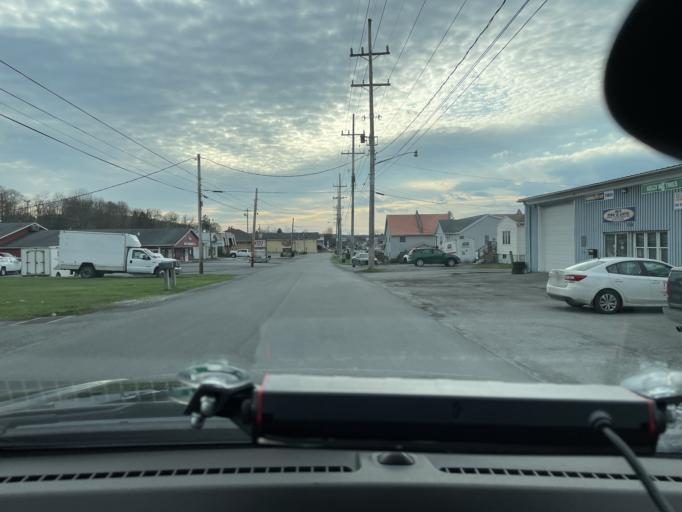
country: US
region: Pennsylvania
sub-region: Cambria County
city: Ebensburg
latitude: 40.4807
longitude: -78.7330
